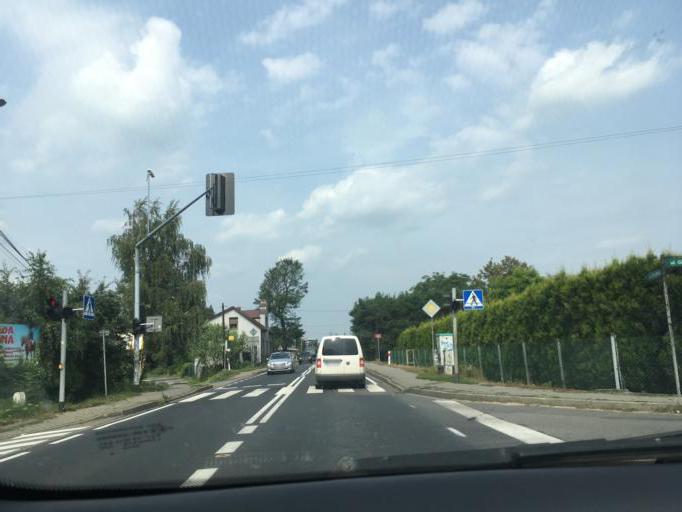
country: PL
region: Lesser Poland Voivodeship
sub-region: Powiat oswiecimski
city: Babice
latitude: 50.0508
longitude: 19.2036
